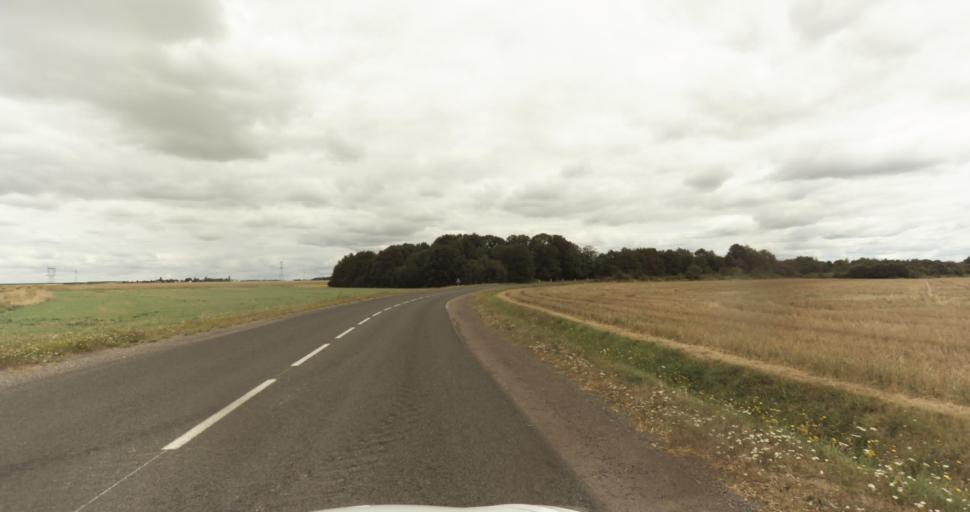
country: FR
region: Haute-Normandie
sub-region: Departement de l'Eure
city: La Madeleine-de-Nonancourt
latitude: 48.8355
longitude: 1.2295
